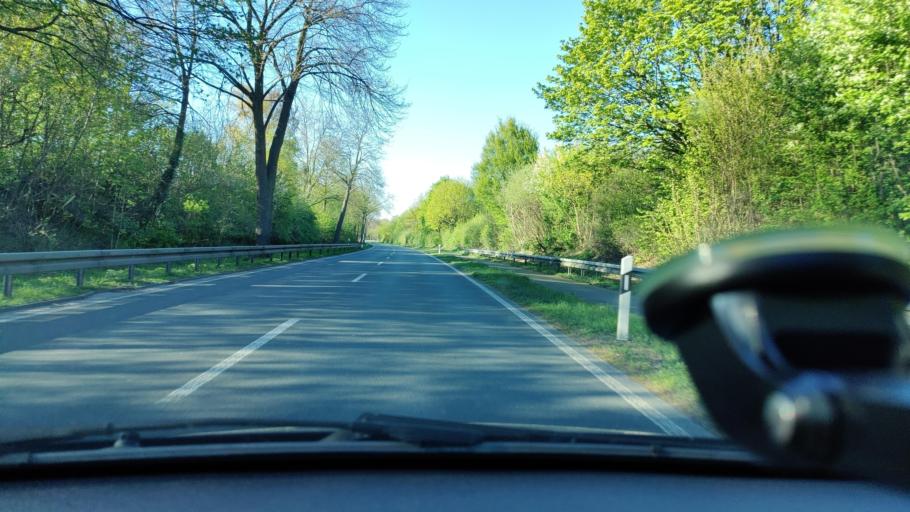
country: DE
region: North Rhine-Westphalia
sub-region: Regierungsbezirk Munster
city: Coesfeld
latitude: 51.9326
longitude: 7.1560
